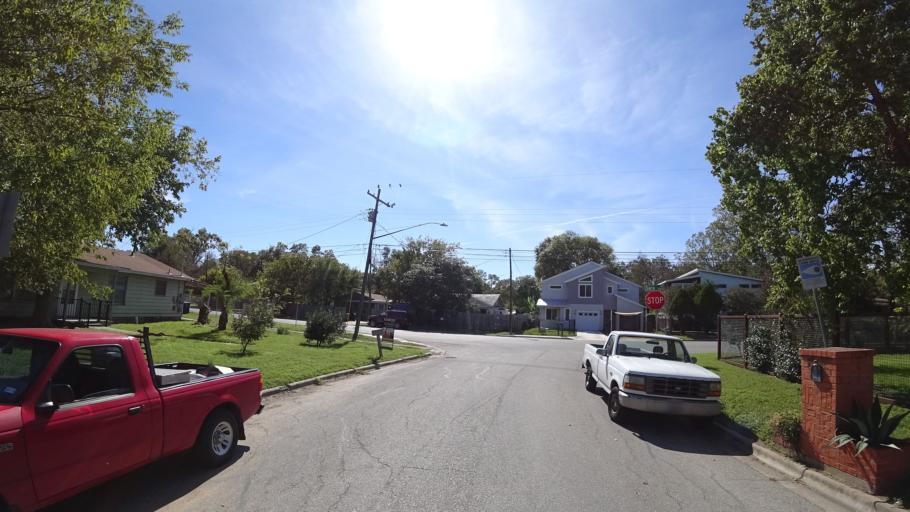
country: US
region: Texas
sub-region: Travis County
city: Austin
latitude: 30.2708
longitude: -97.6894
